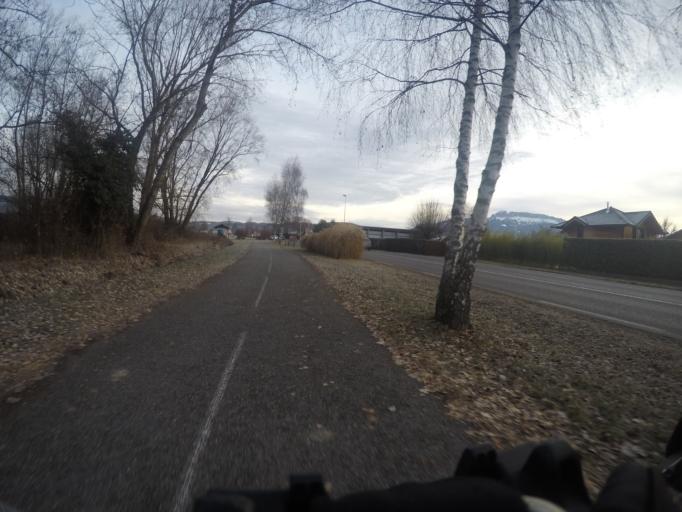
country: FR
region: Rhone-Alpes
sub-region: Departement de la Haute-Savoie
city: Metz-Tessy
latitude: 45.9278
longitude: 6.1055
